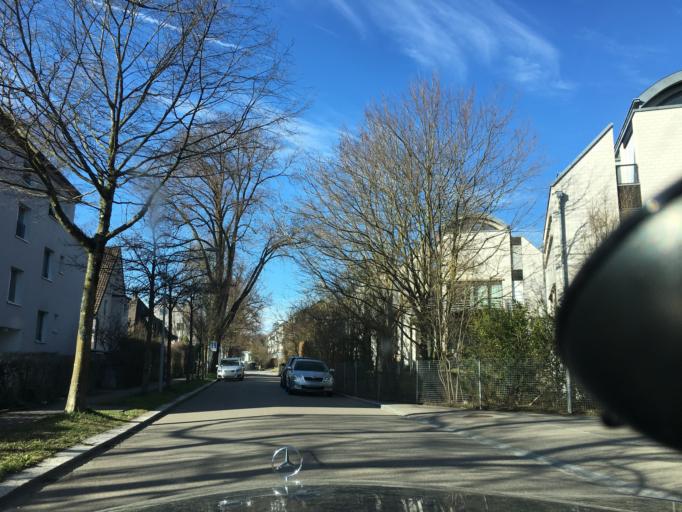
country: CH
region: Zurich
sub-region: Bezirk Zuerich
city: Zuerich (Kreis 7) / Witikon
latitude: 47.3575
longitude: 8.5815
